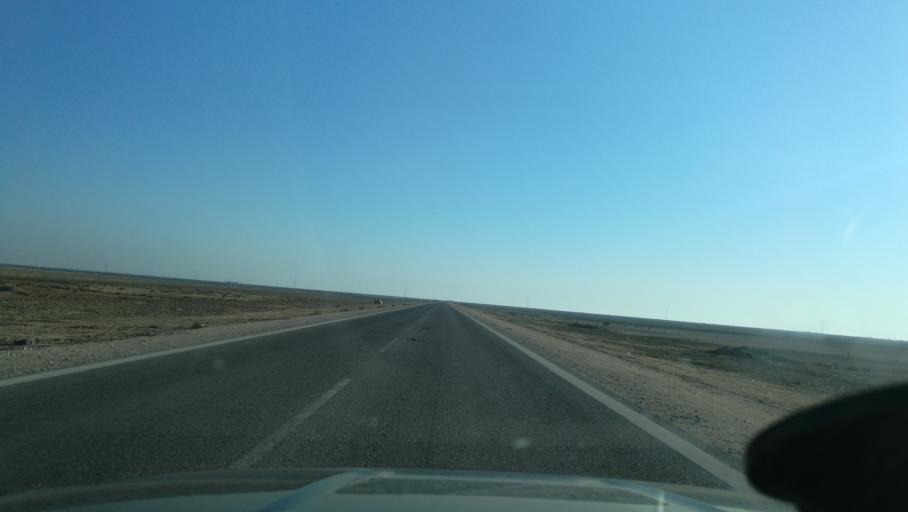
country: IQ
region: Dhi Qar
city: Suq ash Shuyukh
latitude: 30.7987
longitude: 46.3606
